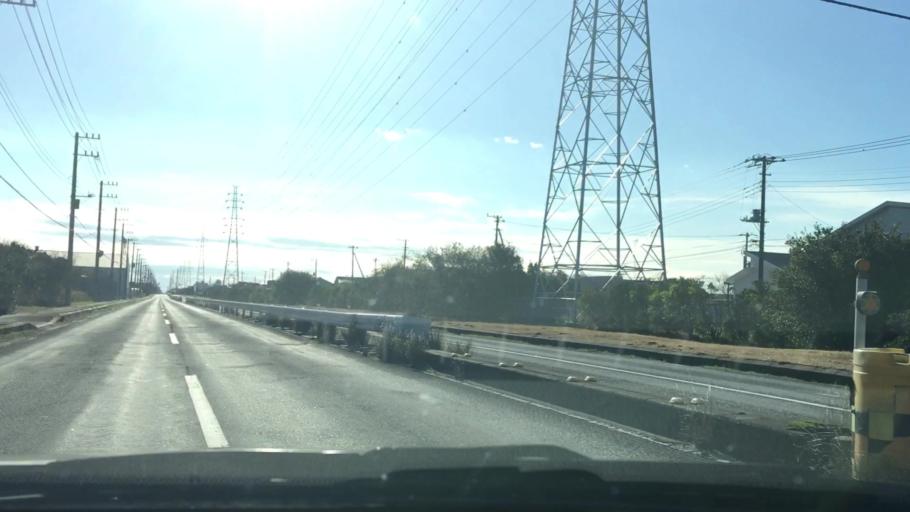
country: JP
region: Chiba
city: Omigawa
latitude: 35.8767
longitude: 140.7187
